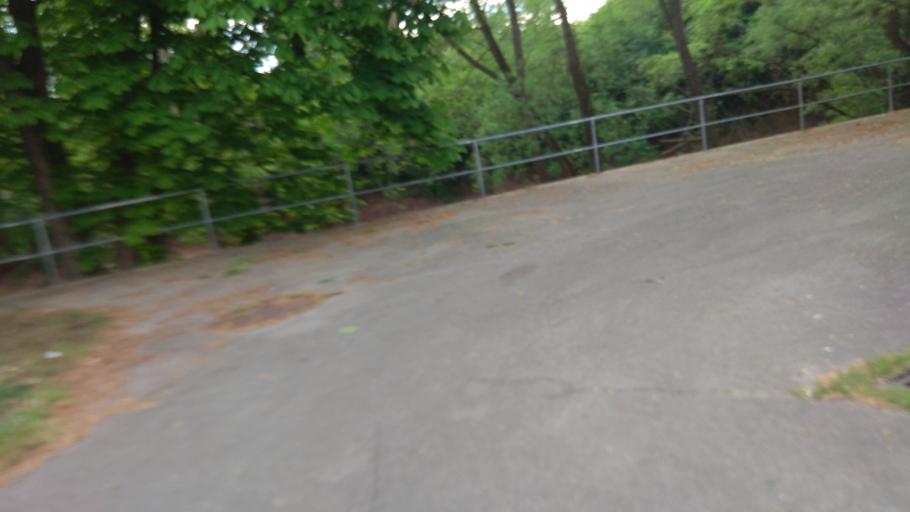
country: DE
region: Baden-Wuerttemberg
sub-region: Tuebingen Region
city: Wannweil
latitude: 48.5097
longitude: 9.1599
